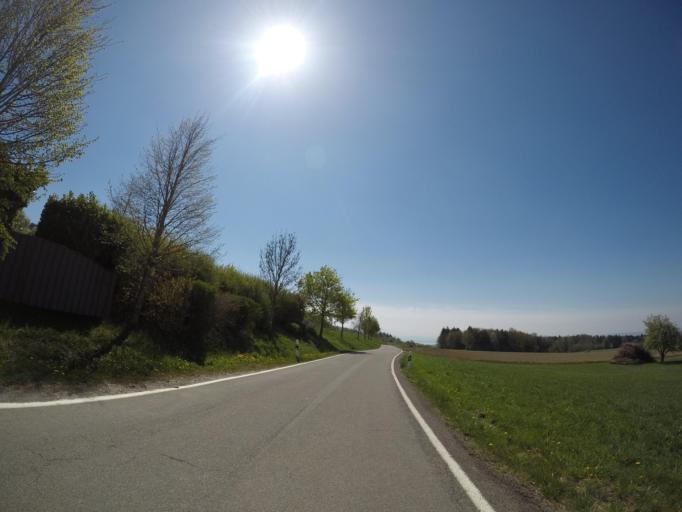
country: DE
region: Baden-Wuerttemberg
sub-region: Tuebingen Region
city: Markdorf
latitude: 47.7472
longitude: 9.3864
